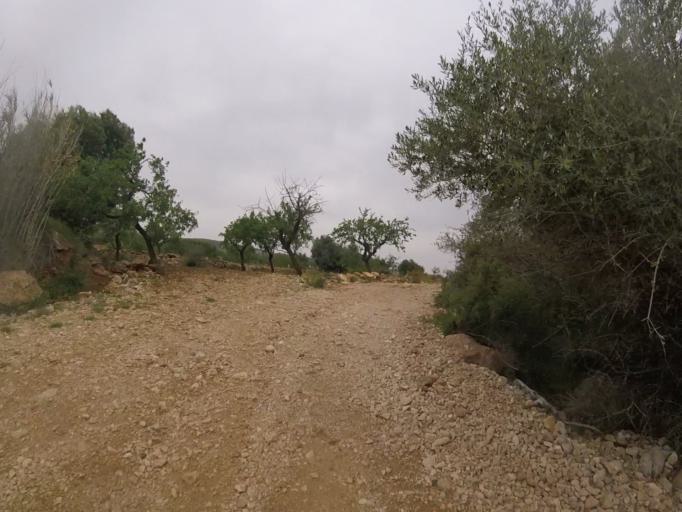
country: ES
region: Valencia
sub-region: Provincia de Castello
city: Alcala de Xivert
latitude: 40.2767
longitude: 0.2556
